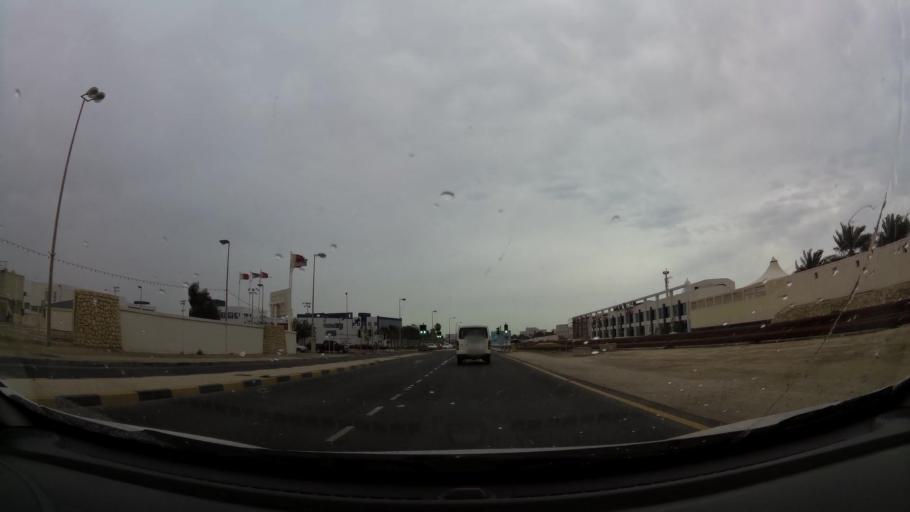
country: BH
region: Central Governorate
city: Madinat Hamad
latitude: 26.1621
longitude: 50.4733
